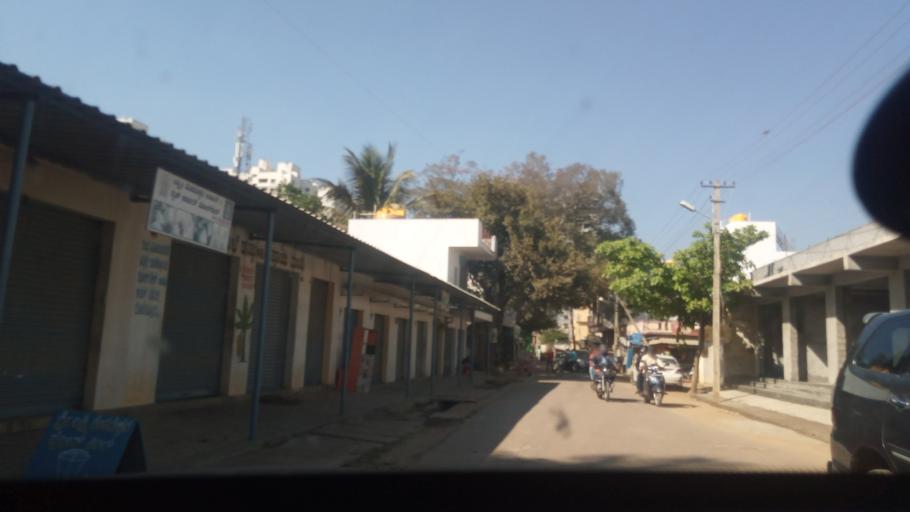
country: IN
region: Karnataka
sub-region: Bangalore Urban
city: Yelahanka
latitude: 13.0427
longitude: 77.5018
